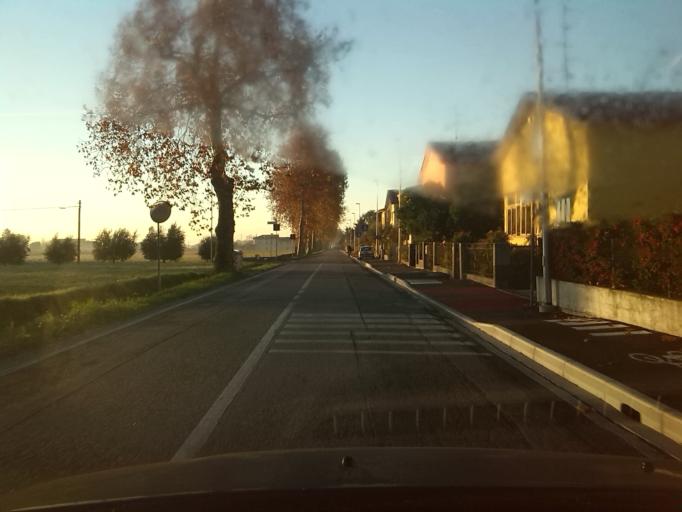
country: IT
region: Friuli Venezia Giulia
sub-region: Provincia di Udine
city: Cividale del Friuli
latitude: 46.0837
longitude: 13.4357
